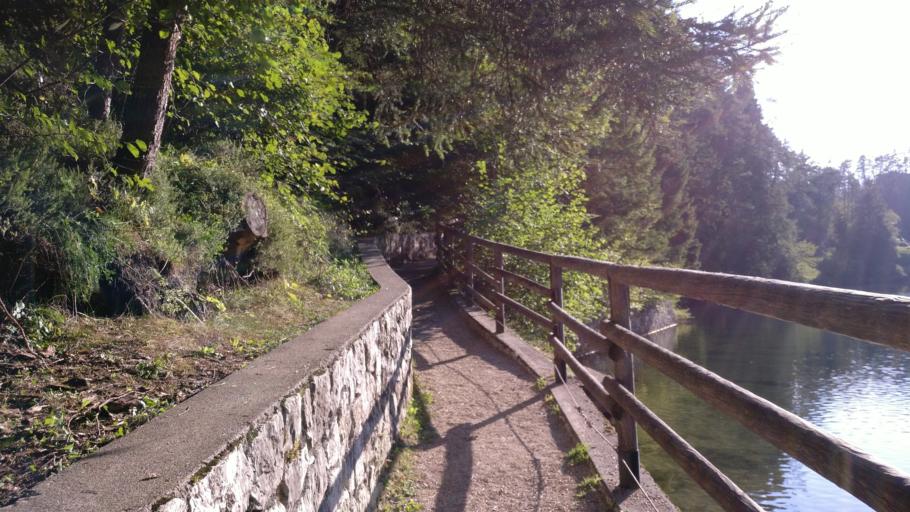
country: IT
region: Trentino-Alto Adige
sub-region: Provincia di Trento
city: Malosco
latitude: 46.4447
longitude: 11.1447
